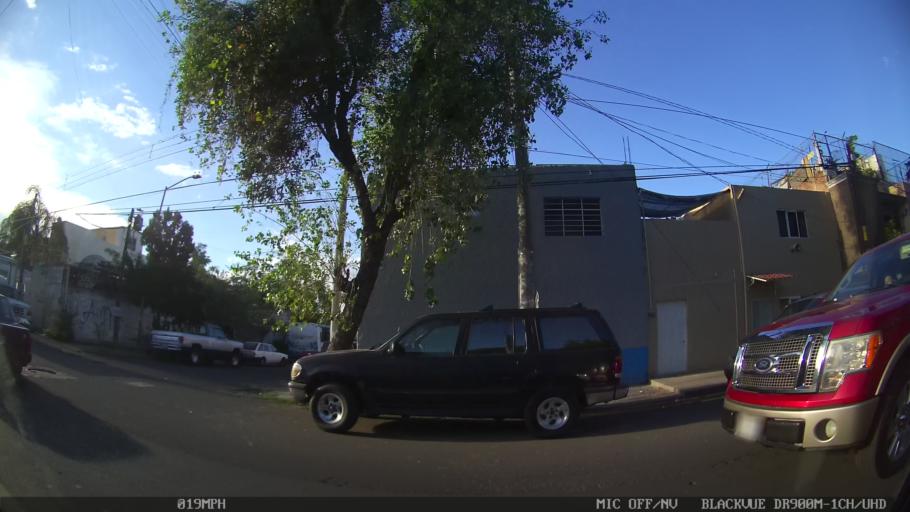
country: MX
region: Jalisco
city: Tlaquepaque
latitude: 20.7091
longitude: -103.3035
